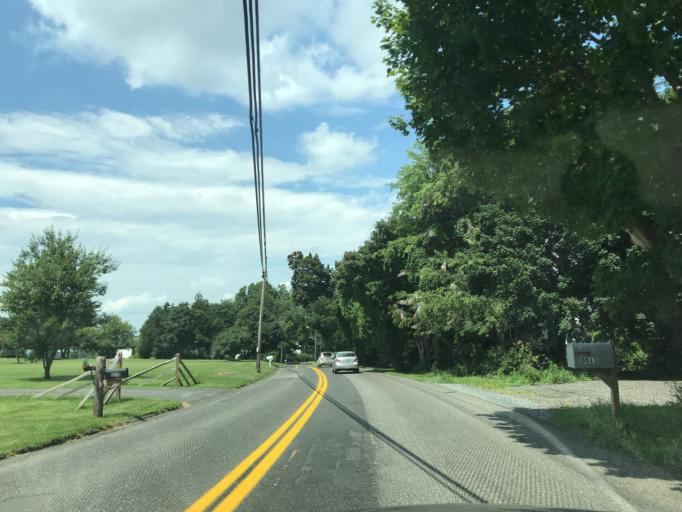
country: US
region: Pennsylvania
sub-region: York County
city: New Freedom
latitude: 39.6724
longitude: -76.7189
